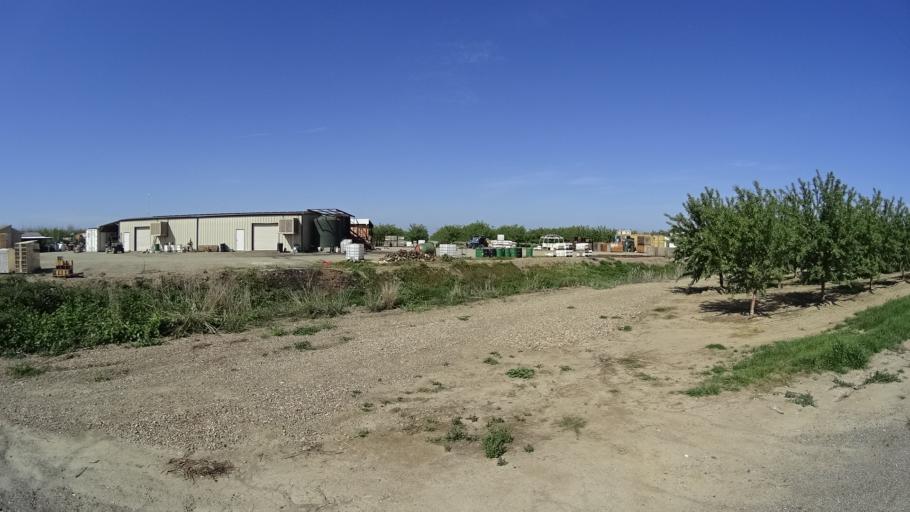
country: US
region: California
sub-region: Glenn County
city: Hamilton City
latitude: 39.6393
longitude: -122.0181
